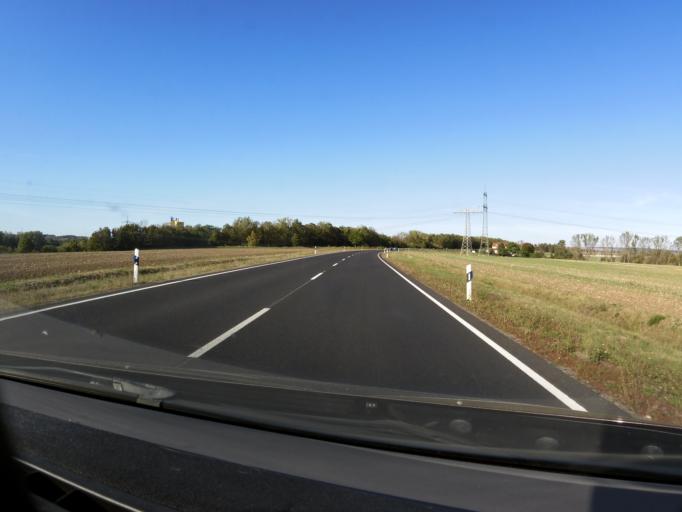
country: DE
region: Saxony-Anhalt
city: Quedlinburg
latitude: 51.7962
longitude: 11.1842
